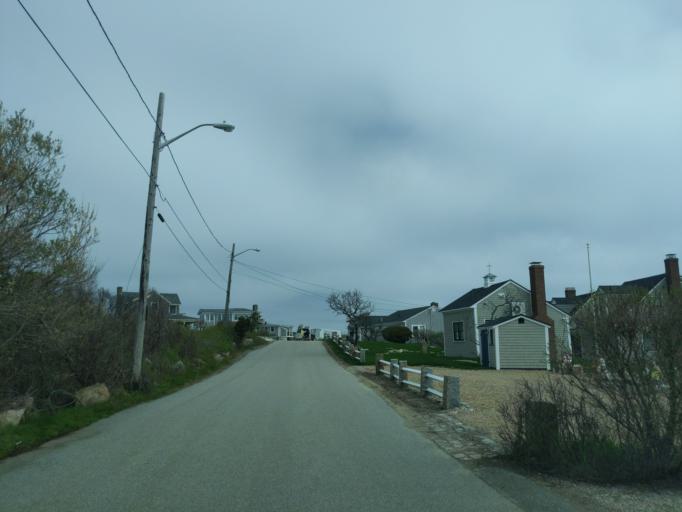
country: US
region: Massachusetts
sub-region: Essex County
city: Rockport
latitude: 42.6474
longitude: -70.5932
